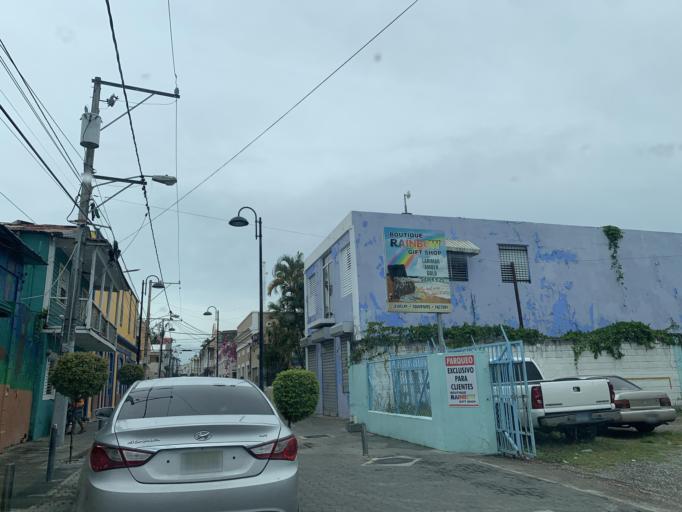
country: DO
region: Puerto Plata
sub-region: Puerto Plata
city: Puerto Plata
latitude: 19.7989
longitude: -70.6947
